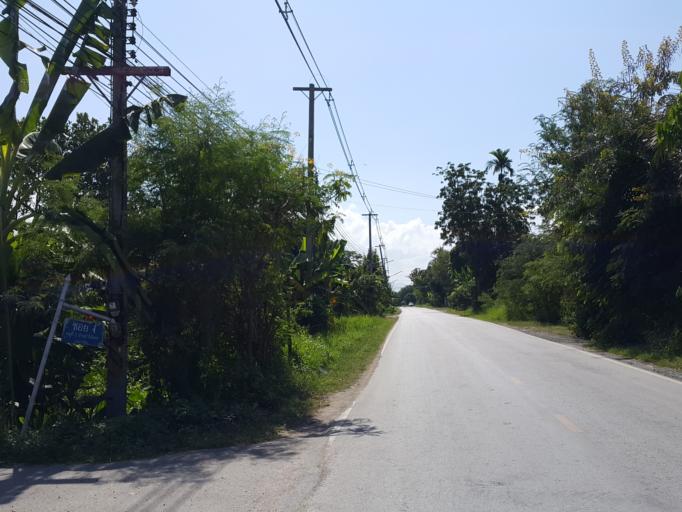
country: TH
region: Chiang Mai
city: San Kamphaeng
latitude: 18.8415
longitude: 99.1489
